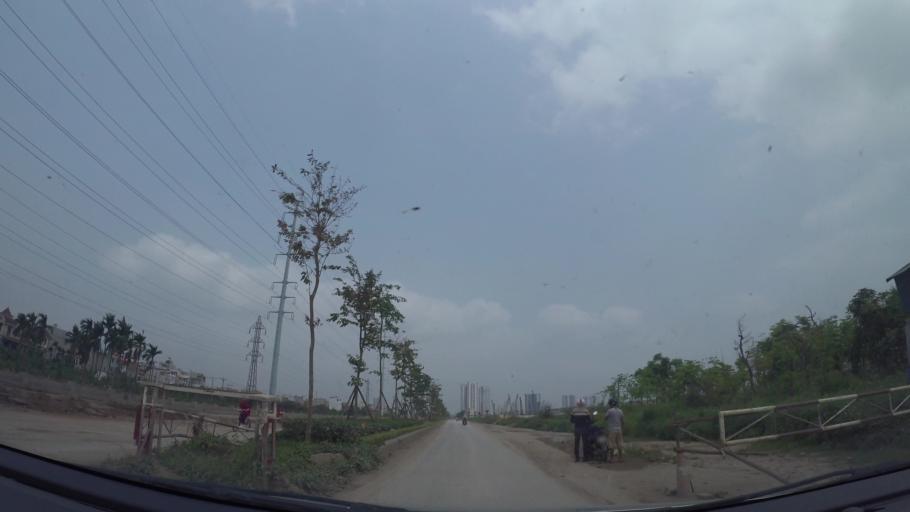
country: VN
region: Ha Noi
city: Tay Ho
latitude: 21.0856
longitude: 105.7976
